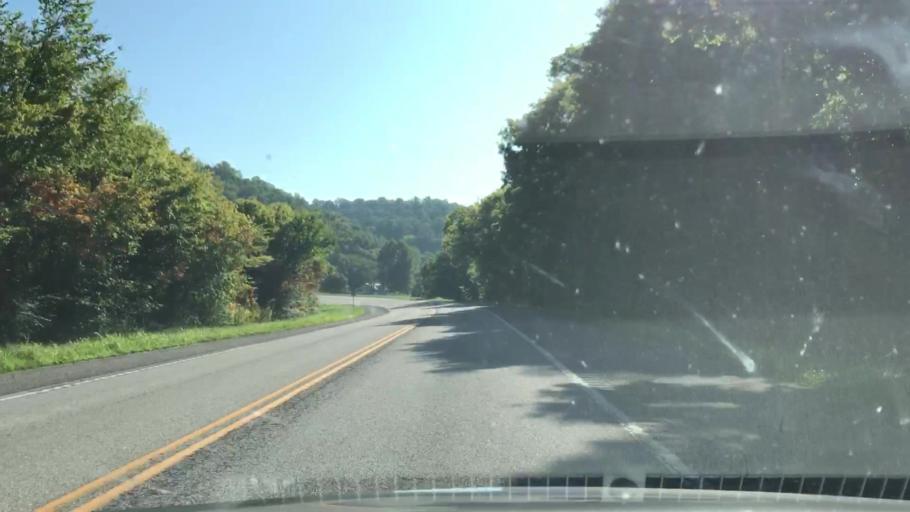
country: US
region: Tennessee
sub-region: Clay County
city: Celina
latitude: 36.5307
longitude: -85.5118
